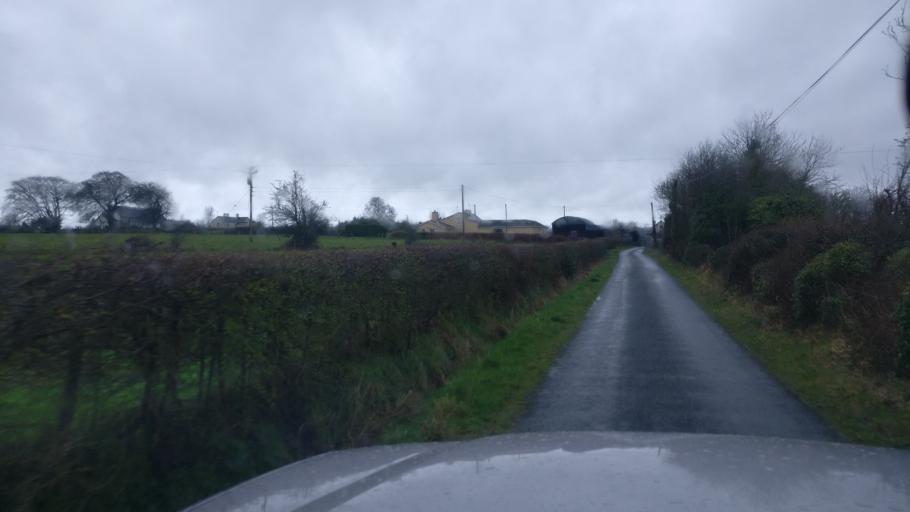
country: IE
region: Connaught
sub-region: County Galway
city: Ballinasloe
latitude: 53.2470
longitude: -8.3511
